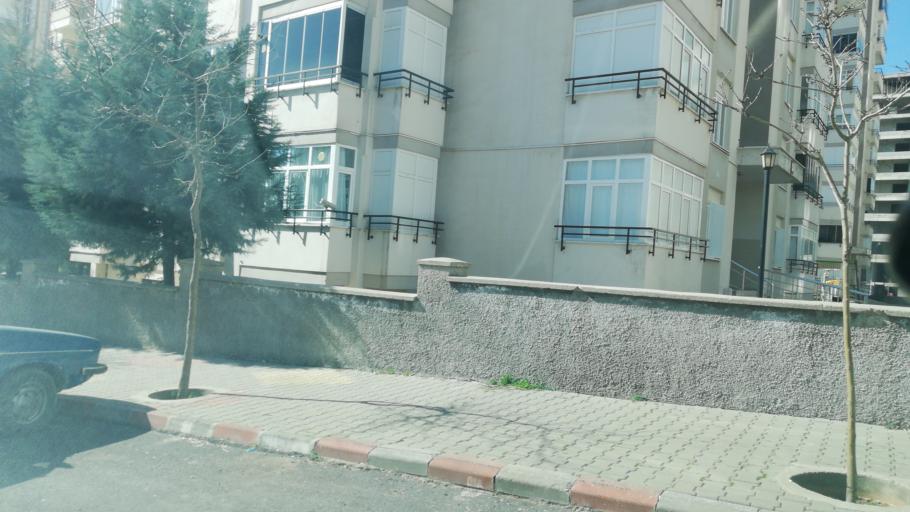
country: TR
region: Kahramanmaras
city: Kahramanmaras
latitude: 37.5825
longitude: 36.8861
